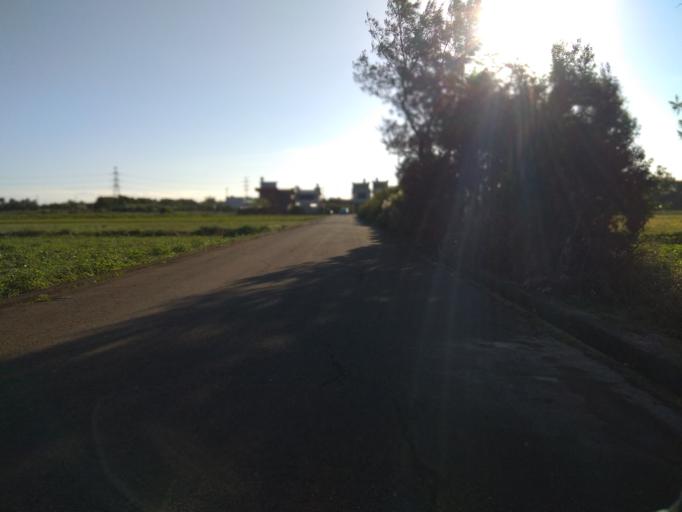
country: TW
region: Taiwan
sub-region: Hsinchu
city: Zhubei
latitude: 24.9948
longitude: 121.0514
